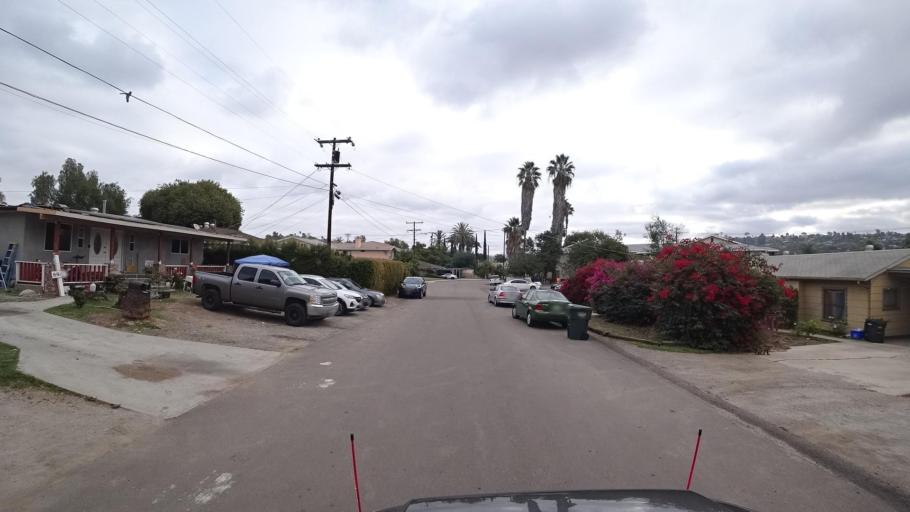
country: US
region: California
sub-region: San Diego County
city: Spring Valley
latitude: 32.7433
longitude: -117.0053
